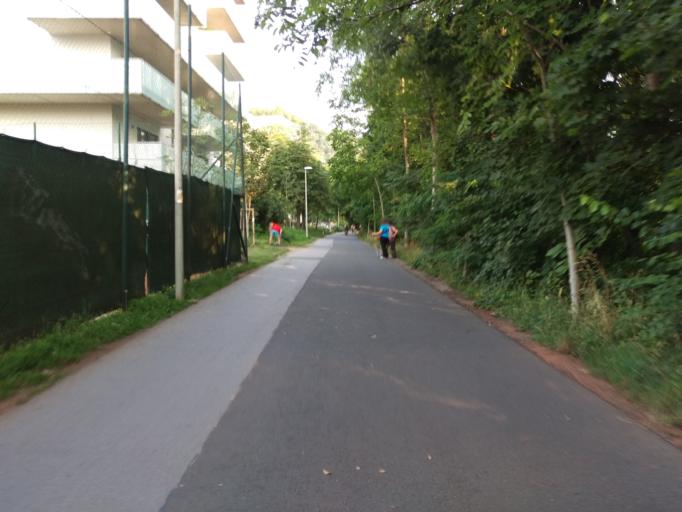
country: AT
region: Styria
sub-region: Graz Stadt
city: Graz
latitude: 47.0812
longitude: 15.4309
